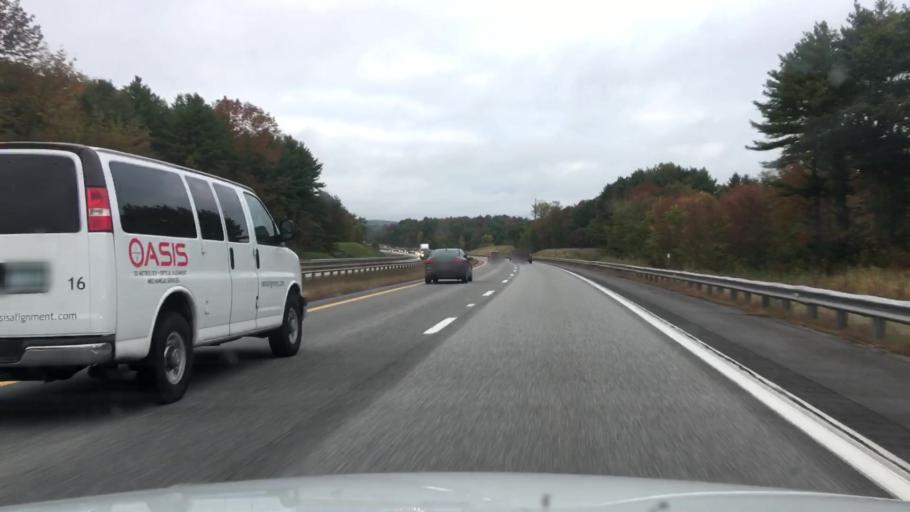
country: US
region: Maine
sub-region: Cumberland County
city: Cumberland Center
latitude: 43.7538
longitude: -70.3042
